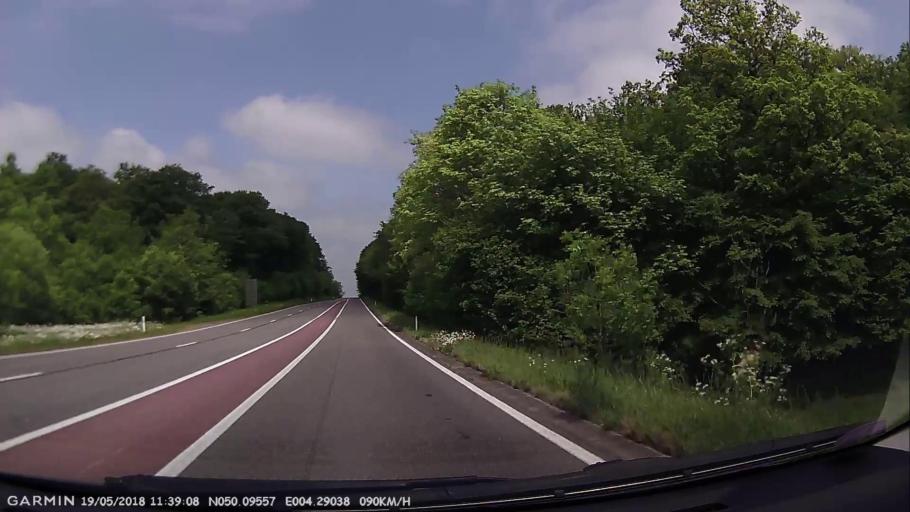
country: BE
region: Wallonia
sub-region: Province du Hainaut
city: Chimay
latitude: 50.0959
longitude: 4.2903
